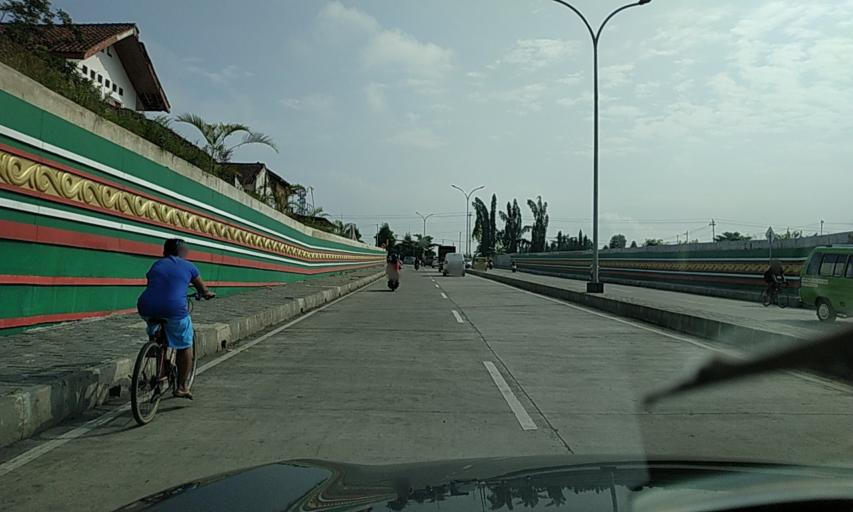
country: ID
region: Central Java
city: Purwokerto
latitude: -7.4250
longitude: 109.2221
